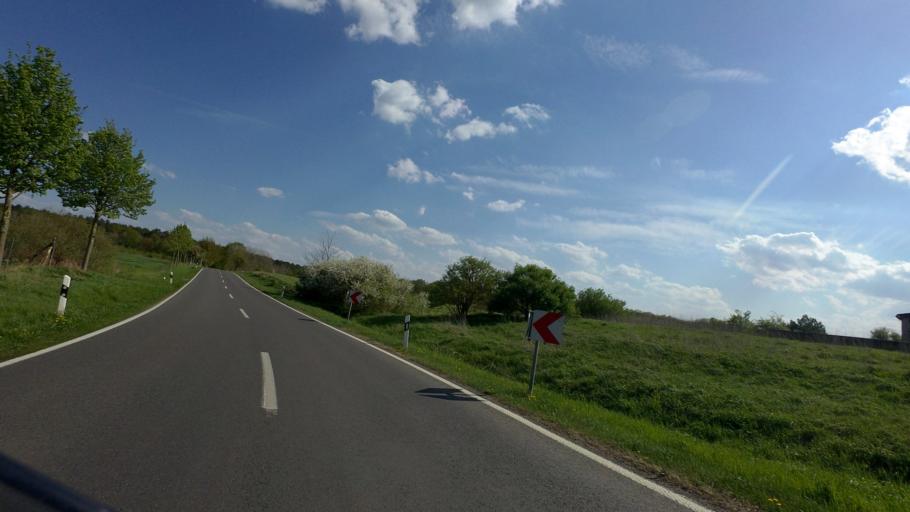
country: DE
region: Brandenburg
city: Templin
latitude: 53.0929
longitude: 13.5018
